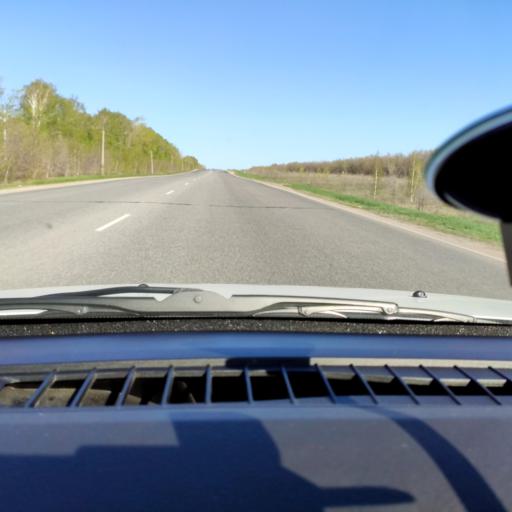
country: RU
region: Samara
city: Dubovyy Umet
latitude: 53.0711
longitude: 50.3619
